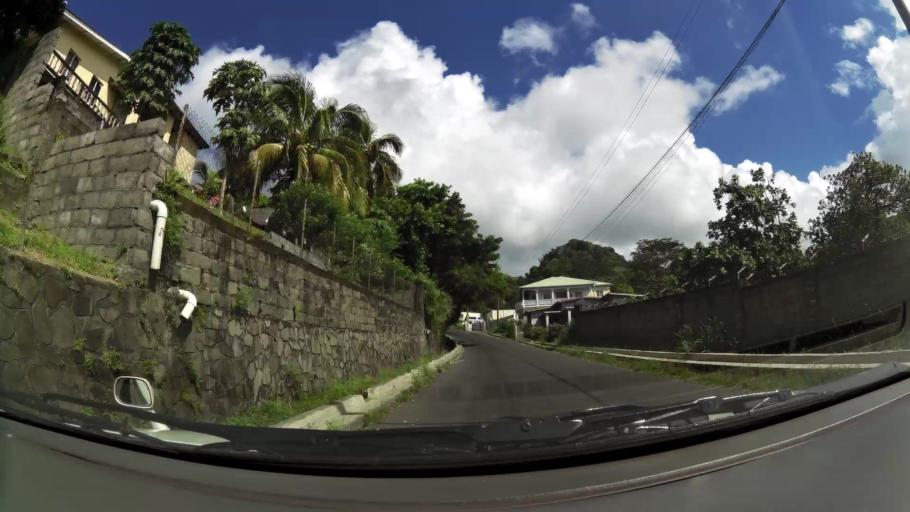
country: VC
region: Saint George
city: Kingstown
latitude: 13.1664
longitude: -61.2287
